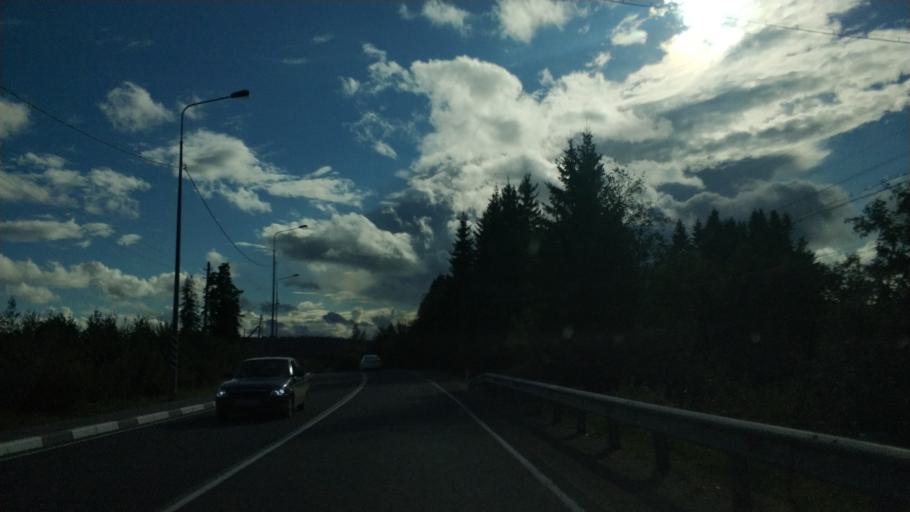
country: RU
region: Republic of Karelia
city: Lakhdenpokh'ya
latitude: 61.5216
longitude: 30.1588
